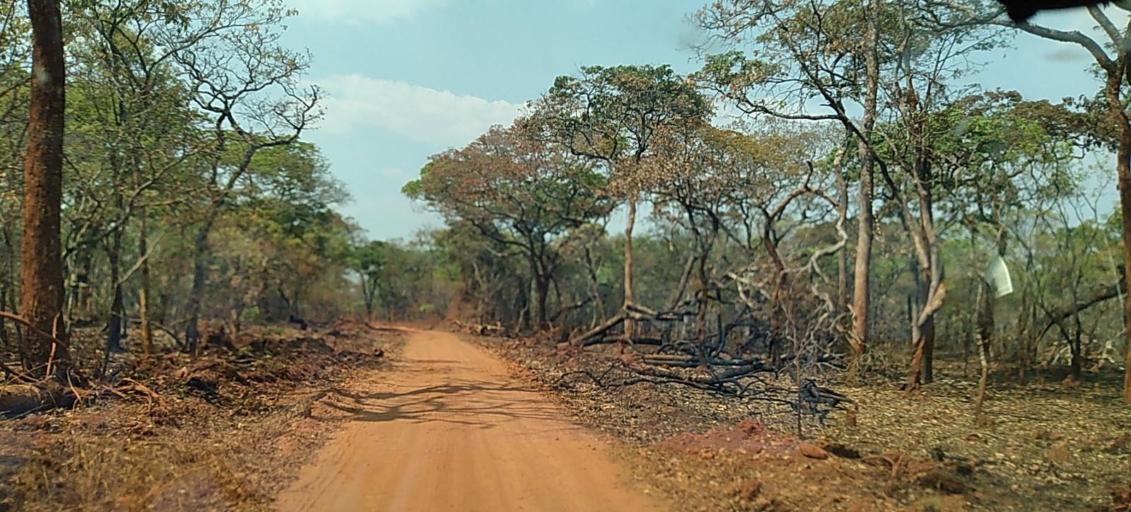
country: ZM
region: North-Western
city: Kasempa
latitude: -13.3159
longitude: 26.0574
